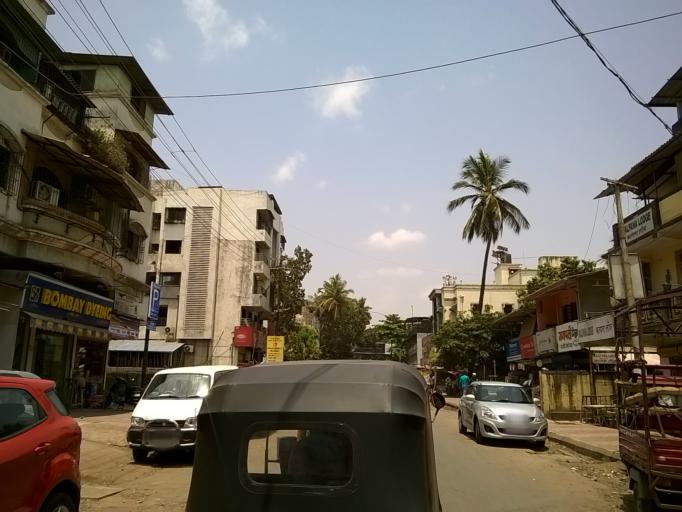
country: IN
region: Maharashtra
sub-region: Raigarh
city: Panvel
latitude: 18.9878
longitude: 73.1143
